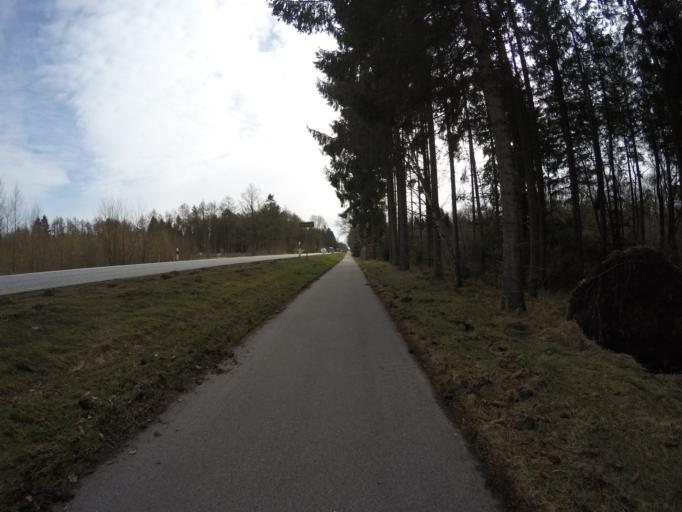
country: DE
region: Schleswig-Holstein
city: Lentfohrden
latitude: 53.8354
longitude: 9.8845
